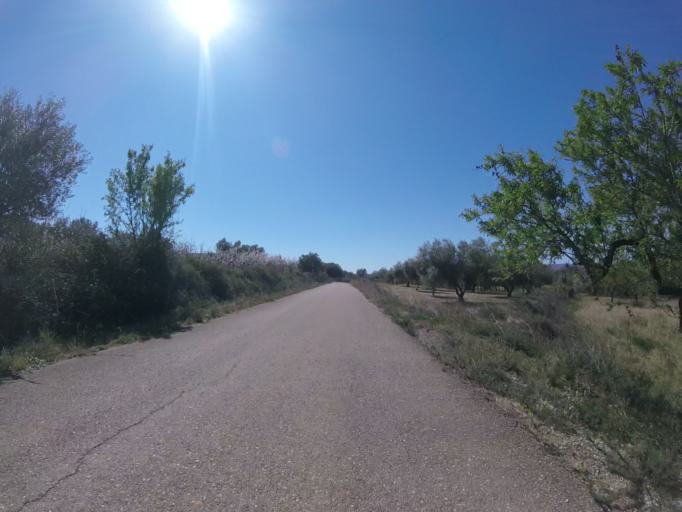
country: ES
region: Valencia
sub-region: Provincia de Castello
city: Cuevas de Vinroma
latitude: 40.3842
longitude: 0.1570
